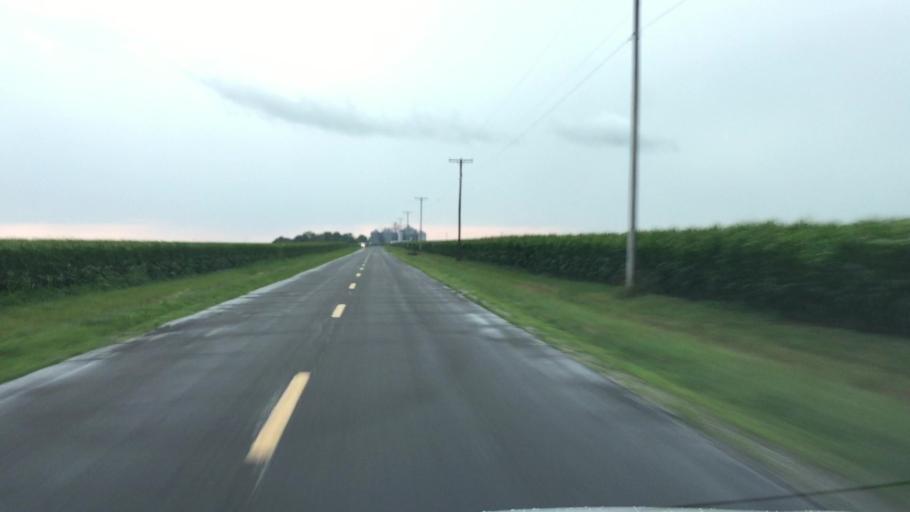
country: US
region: Illinois
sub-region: Hancock County
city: Carthage
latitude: 40.5203
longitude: -91.1487
